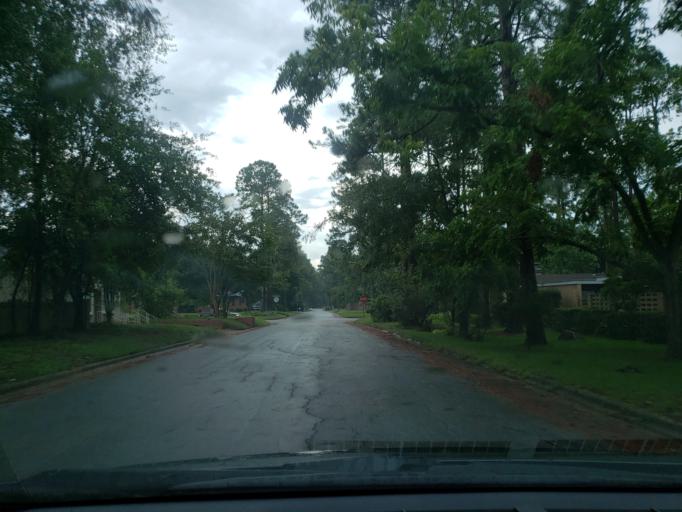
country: US
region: Georgia
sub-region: Dougherty County
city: Albany
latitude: 31.6057
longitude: -84.1870
